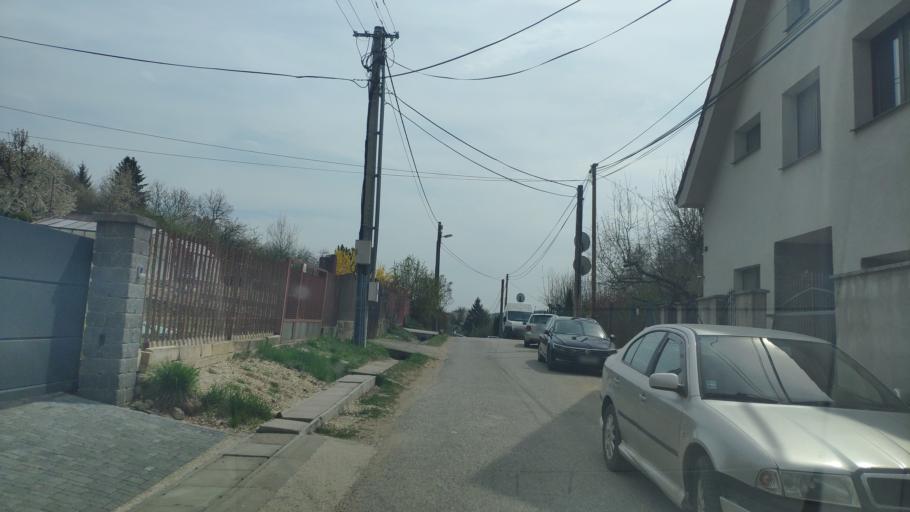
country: SK
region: Kosicky
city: Kosice
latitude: 48.7202
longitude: 21.1946
